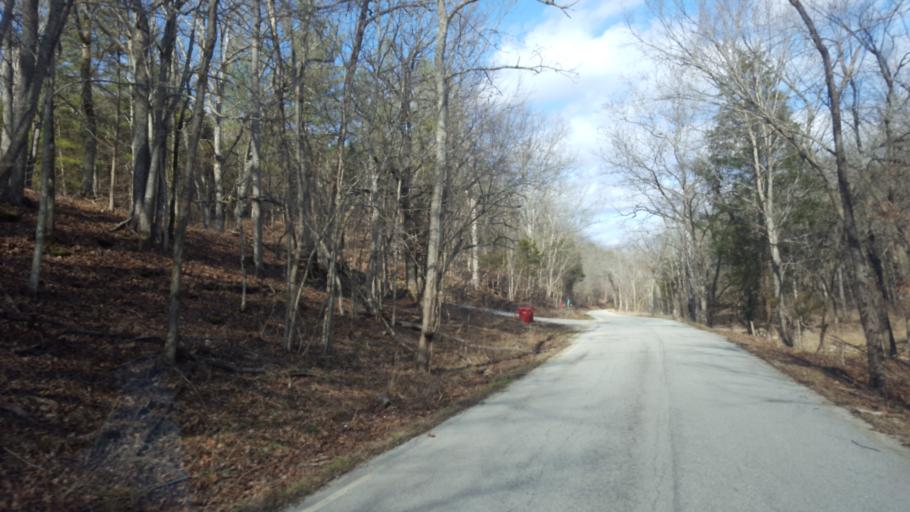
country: US
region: Kentucky
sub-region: Franklin County
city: Frankfort
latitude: 38.3062
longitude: -84.8955
